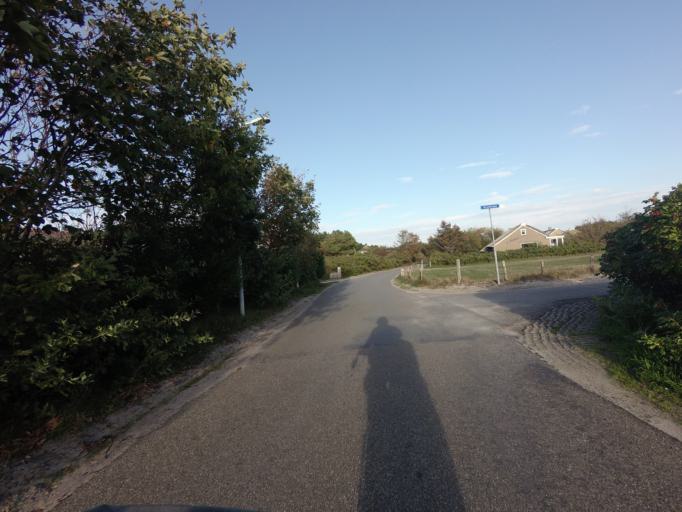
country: NL
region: Friesland
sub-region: Gemeente Ameland
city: Nes
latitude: 53.4582
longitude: 5.8015
